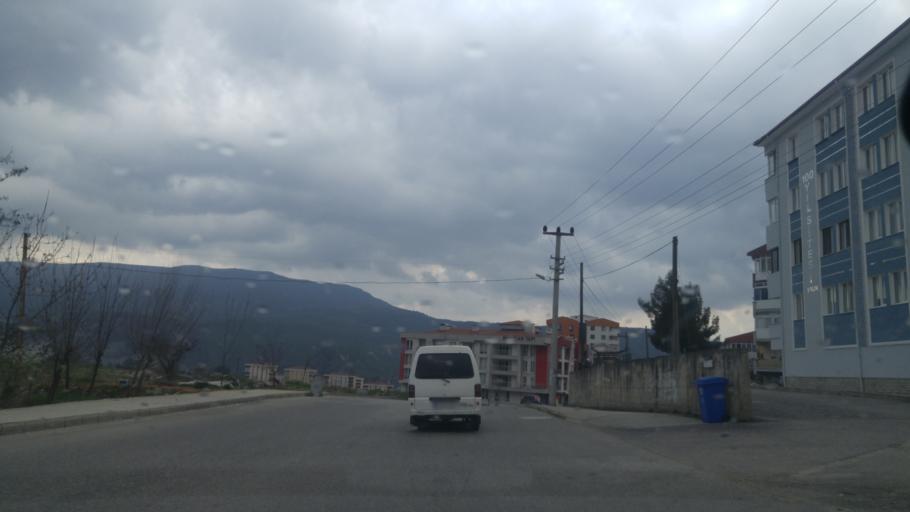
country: TR
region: Karabuk
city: Safranbolu
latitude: 41.2230
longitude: 32.6725
